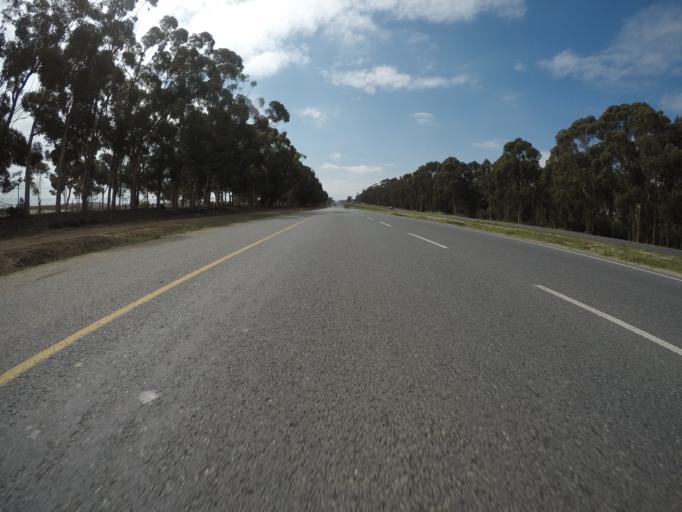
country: ZA
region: Western Cape
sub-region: City of Cape Town
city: Sunset Beach
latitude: -33.7733
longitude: 18.5481
